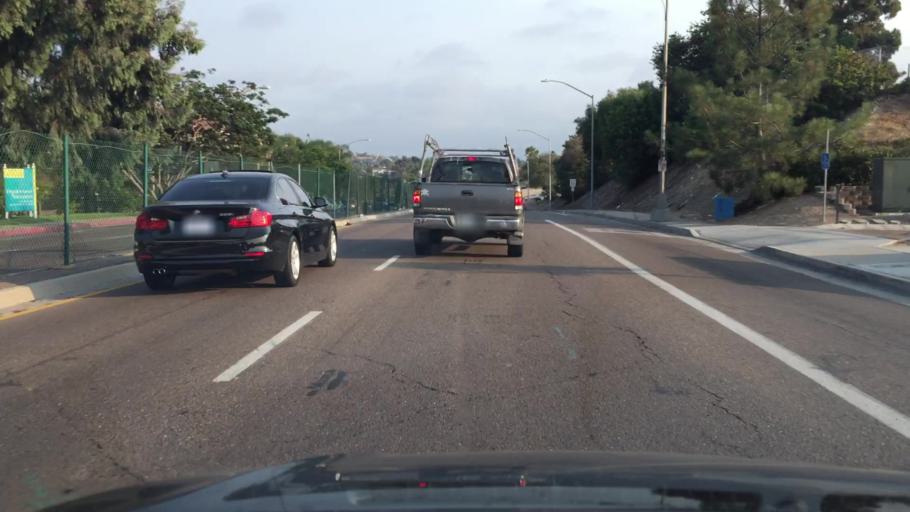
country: US
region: California
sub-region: San Diego County
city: Lemon Grove
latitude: 32.7517
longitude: -117.0795
